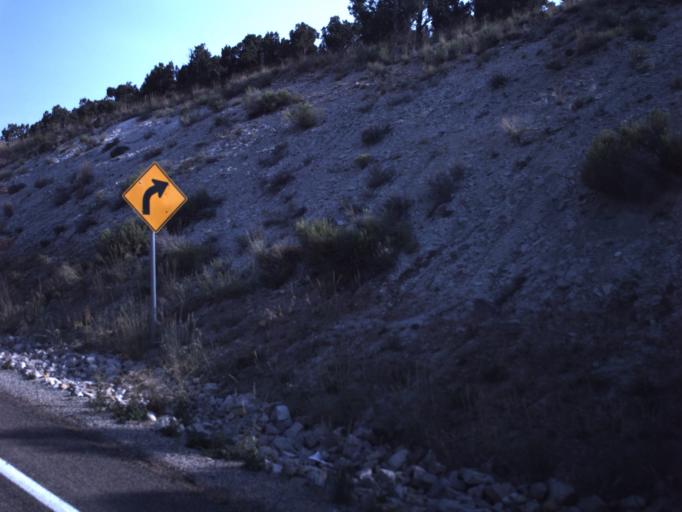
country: US
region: Utah
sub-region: Uintah County
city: Vernal
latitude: 40.6261
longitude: -109.4746
